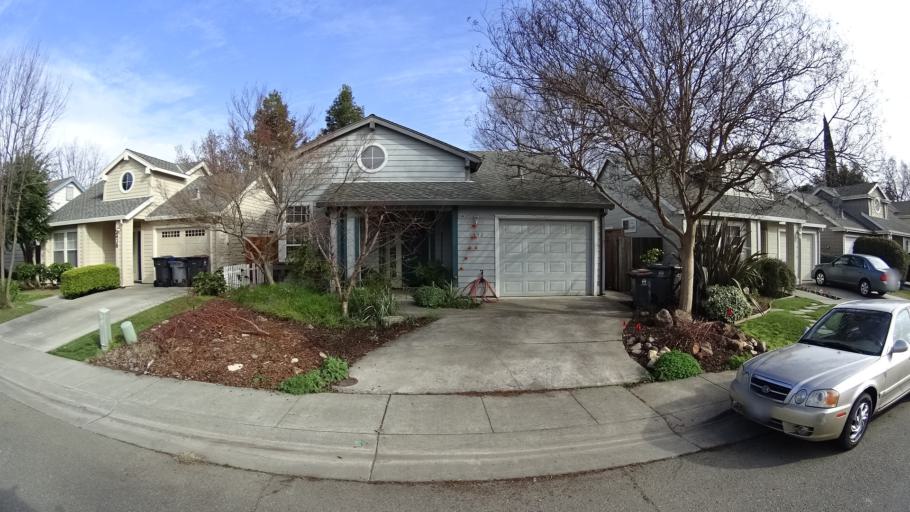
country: US
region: California
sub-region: Yolo County
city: Davis
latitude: 38.5441
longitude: -121.7203
